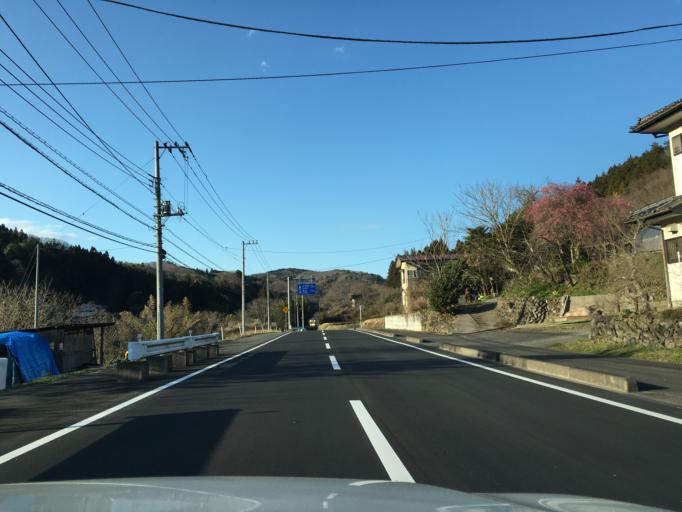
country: JP
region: Tochigi
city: Karasuyama
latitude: 36.7580
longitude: 140.2022
